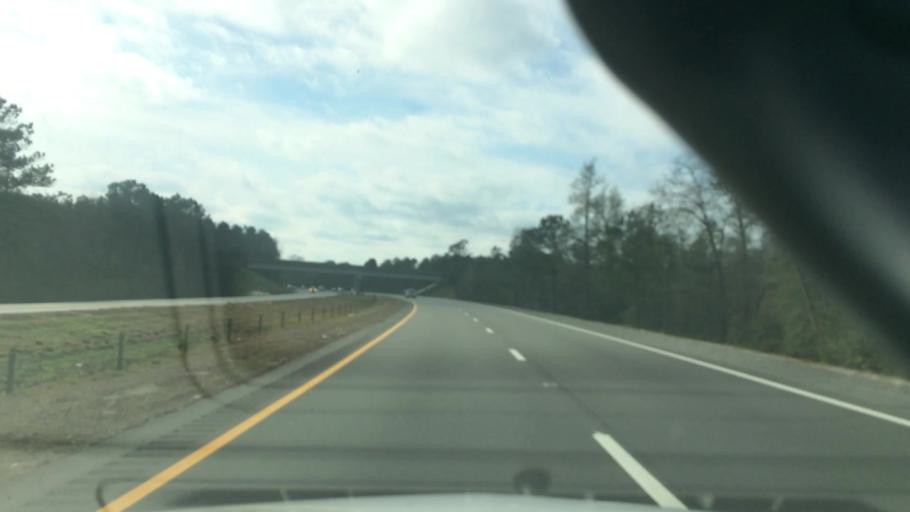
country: US
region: North Carolina
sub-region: New Hanover County
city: Wrightsboro
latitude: 34.3183
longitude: -77.9406
